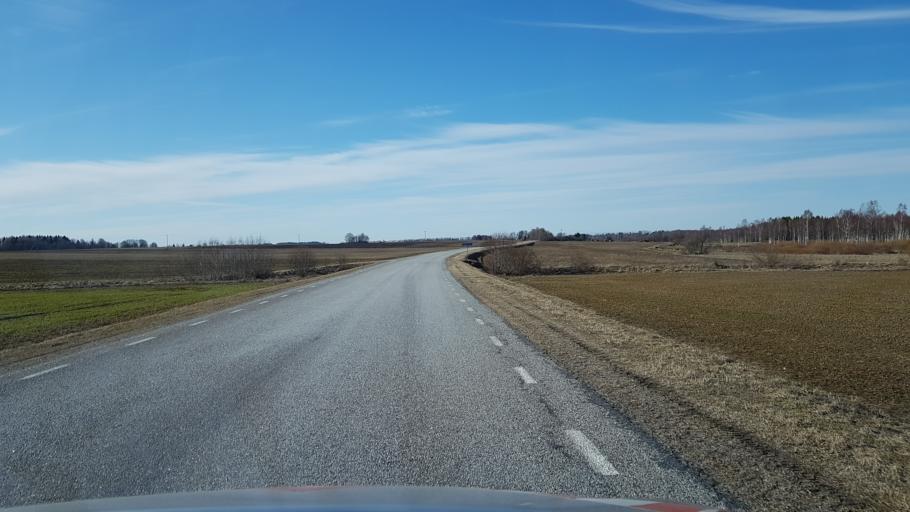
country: EE
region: Laeaene-Virumaa
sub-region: Kadrina vald
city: Kadrina
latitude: 59.3164
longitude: 26.1495
